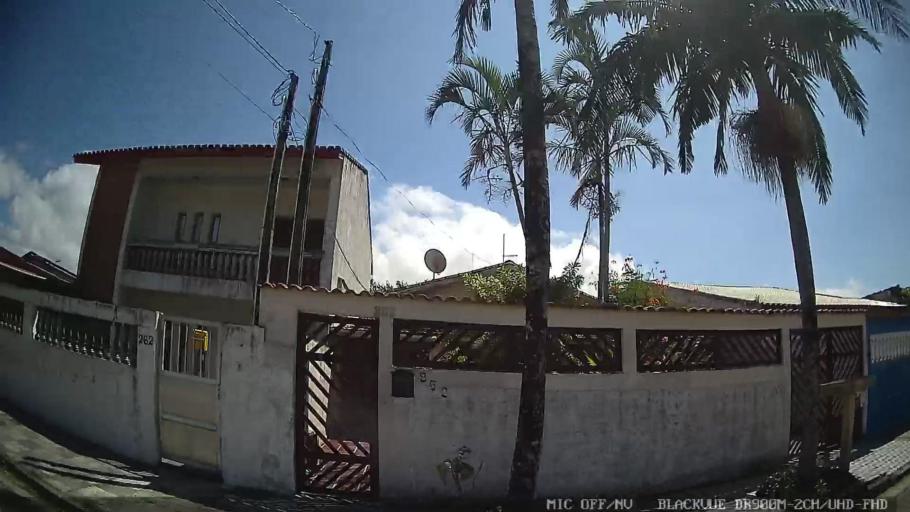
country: BR
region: Sao Paulo
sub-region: Peruibe
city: Peruibe
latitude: -24.3209
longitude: -47.0084
